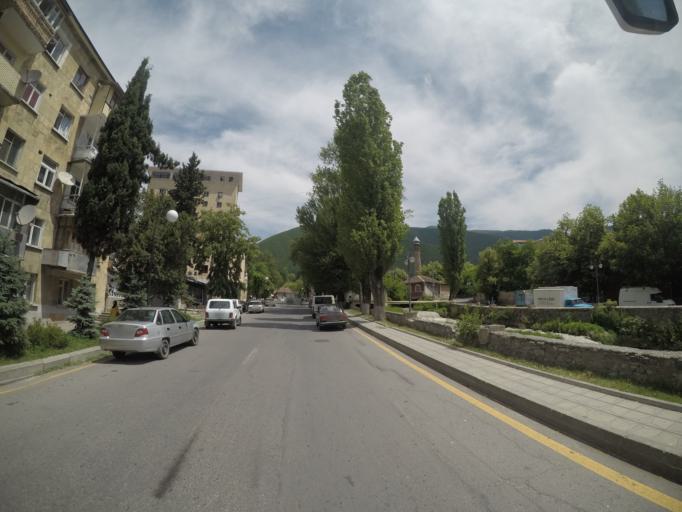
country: AZ
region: Shaki City
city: Sheki
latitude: 41.2016
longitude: 47.1799
